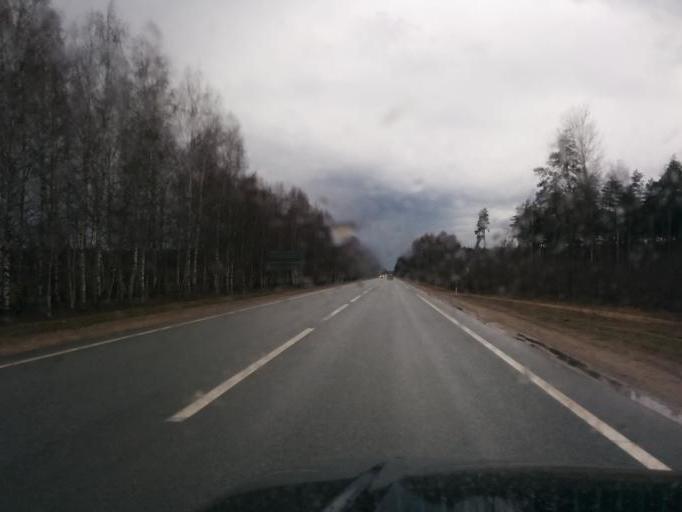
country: LV
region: Babite
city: Pinki
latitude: 56.8814
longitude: 23.9490
